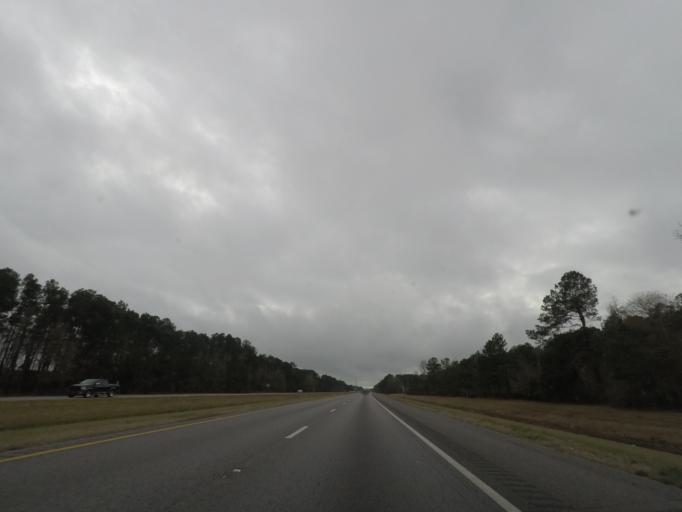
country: US
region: South Carolina
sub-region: Orangeburg County
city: Holly Hill
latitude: 33.4410
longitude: -80.4836
